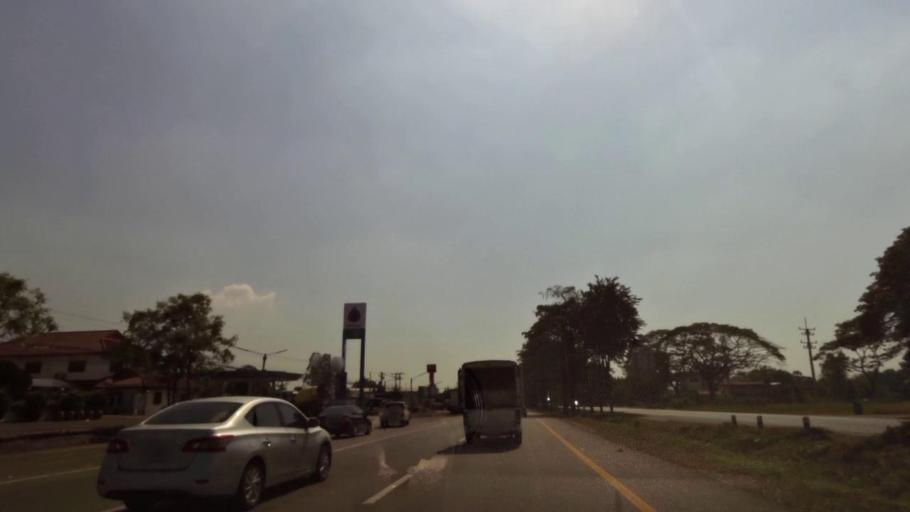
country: TH
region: Phichit
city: Bueng Na Rang
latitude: 16.1193
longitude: 100.1257
